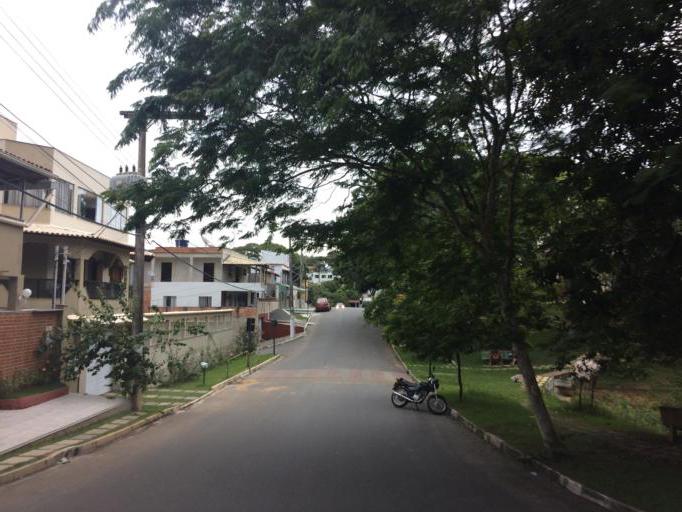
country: BR
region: Espirito Santo
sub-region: Guarapari
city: Guarapari
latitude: -20.6546
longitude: -40.5063
